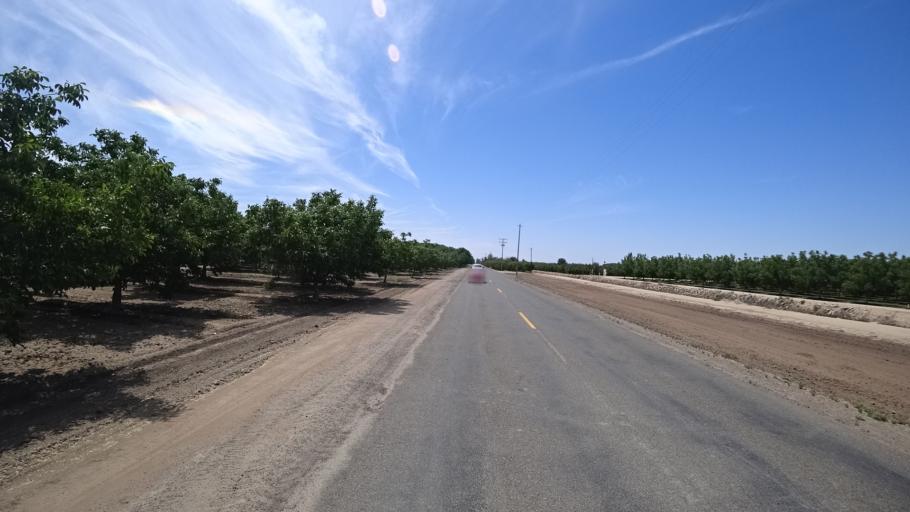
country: US
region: California
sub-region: Kings County
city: Lucerne
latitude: 36.3691
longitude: -119.6910
